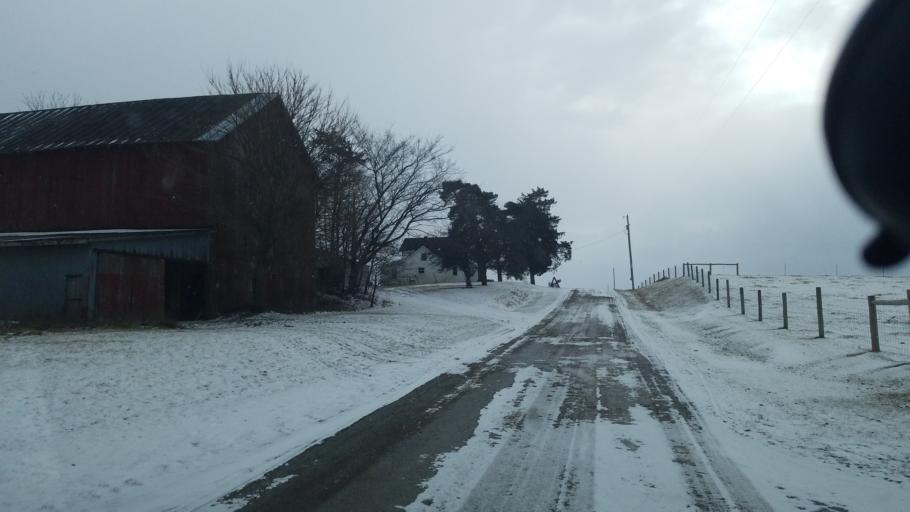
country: US
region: Ohio
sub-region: Morrow County
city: Mount Gilead
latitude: 40.5558
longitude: -82.7152
